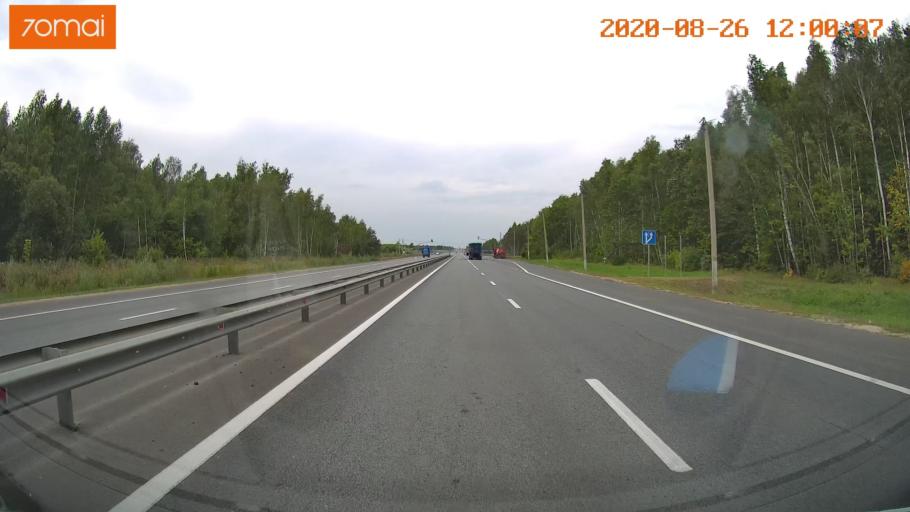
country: RU
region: Rjazan
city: Kiritsy
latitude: 54.2865
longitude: 40.2815
